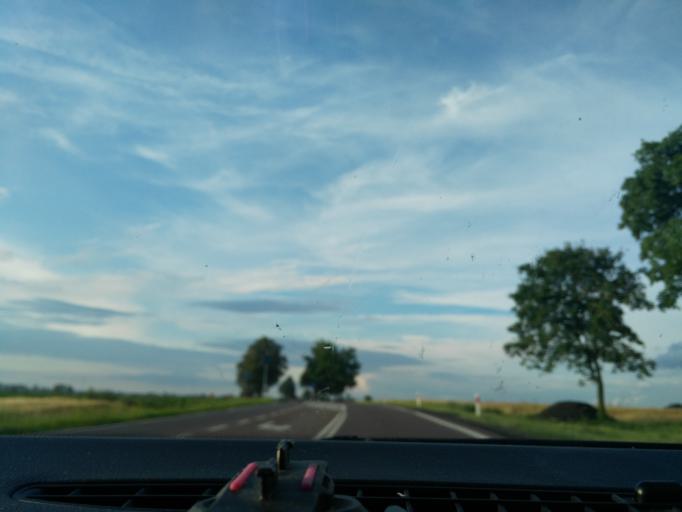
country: PL
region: Lublin Voivodeship
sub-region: Powiat krasnicki
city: Wilkolaz
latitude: 51.0396
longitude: 22.3781
